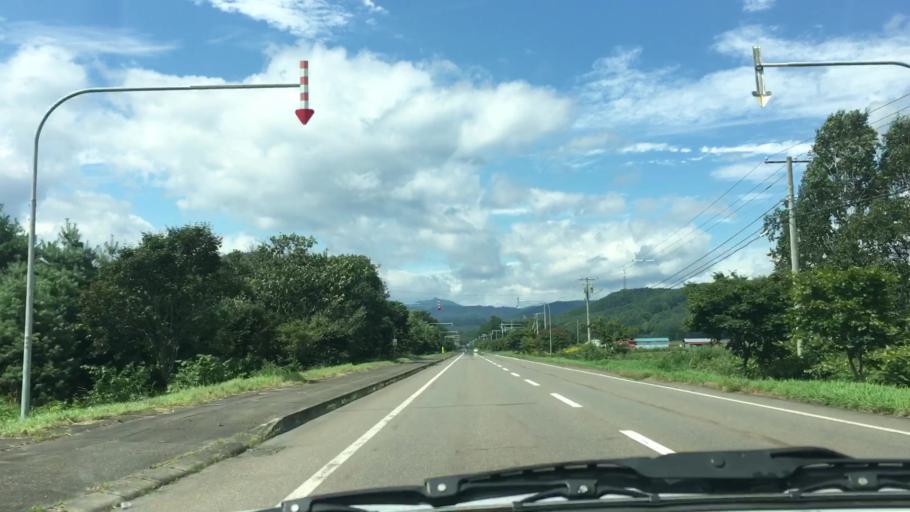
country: JP
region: Hokkaido
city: Otofuke
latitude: 43.3125
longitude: 143.3071
